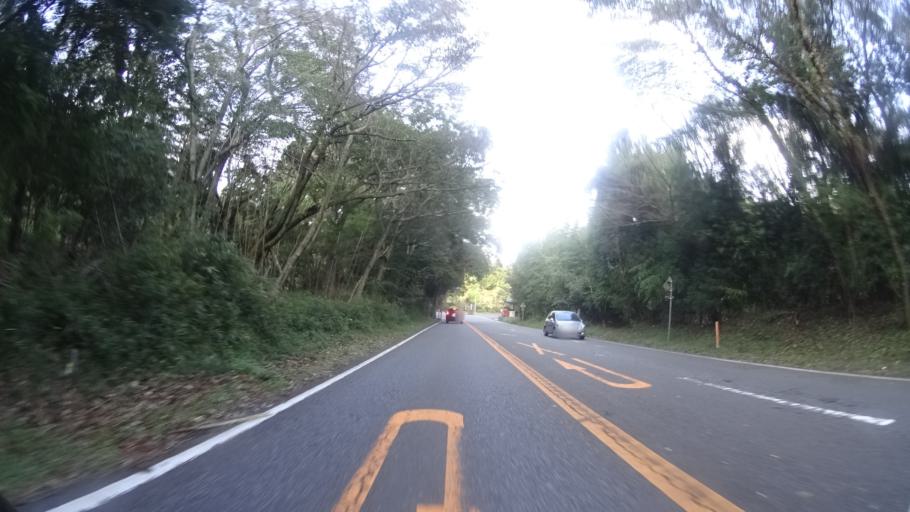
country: JP
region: Oita
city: Beppu
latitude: 33.2742
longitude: 131.4440
